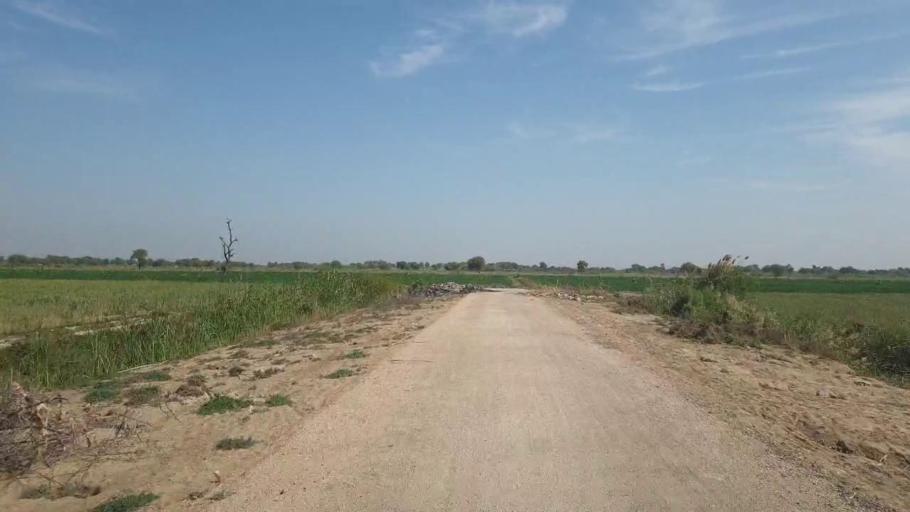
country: PK
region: Sindh
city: Samaro
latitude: 25.3744
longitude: 69.2615
